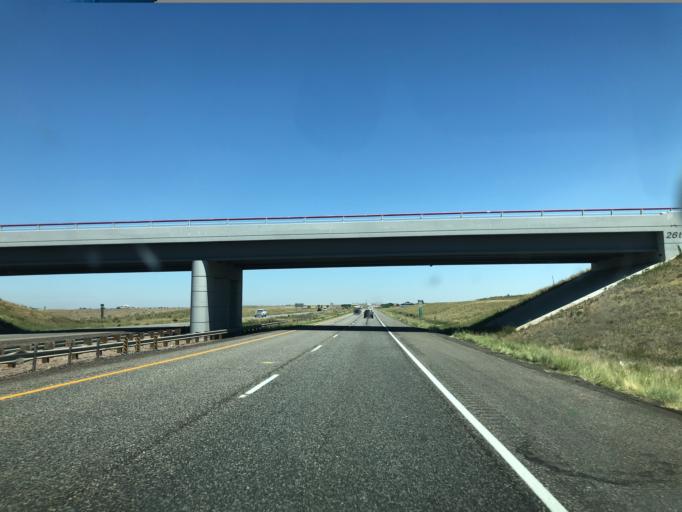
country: US
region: Colorado
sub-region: Adams County
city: Aurora
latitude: 39.7539
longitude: -104.7165
